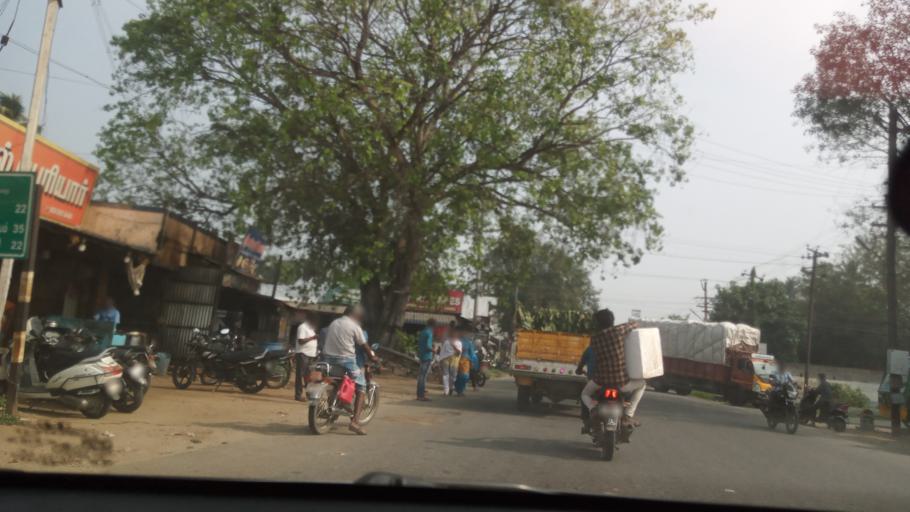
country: IN
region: Tamil Nadu
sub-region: Erode
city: Punjai Puliyampatti
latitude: 11.3421
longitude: 77.1605
